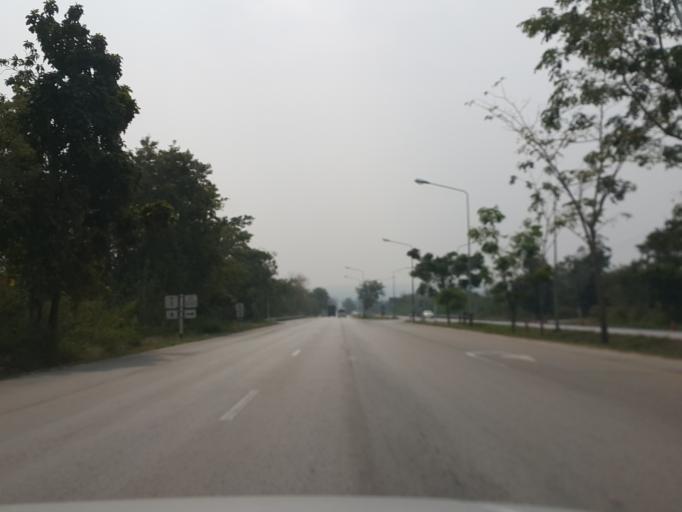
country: TH
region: Lampang
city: Ko Kha
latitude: 18.0938
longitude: 99.3974
